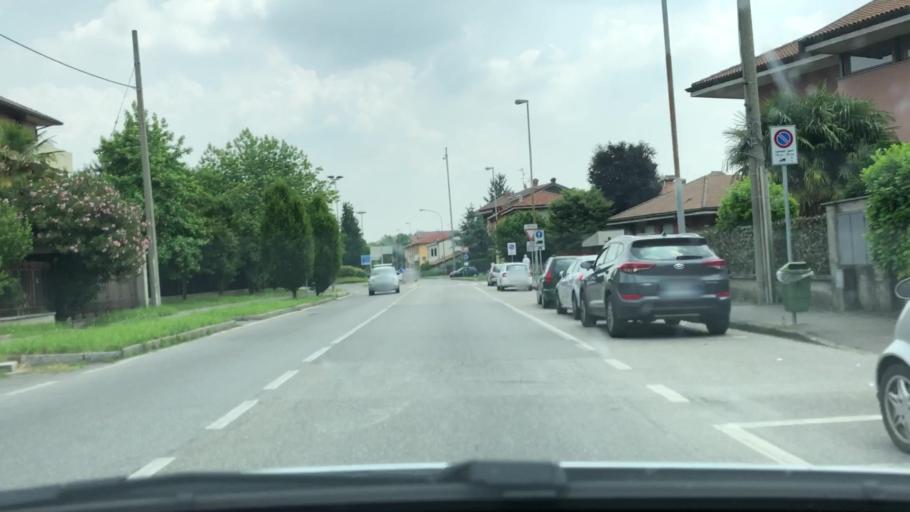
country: IT
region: Lombardy
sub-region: Provincia di Monza e Brianza
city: Desio
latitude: 45.6235
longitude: 9.1954
